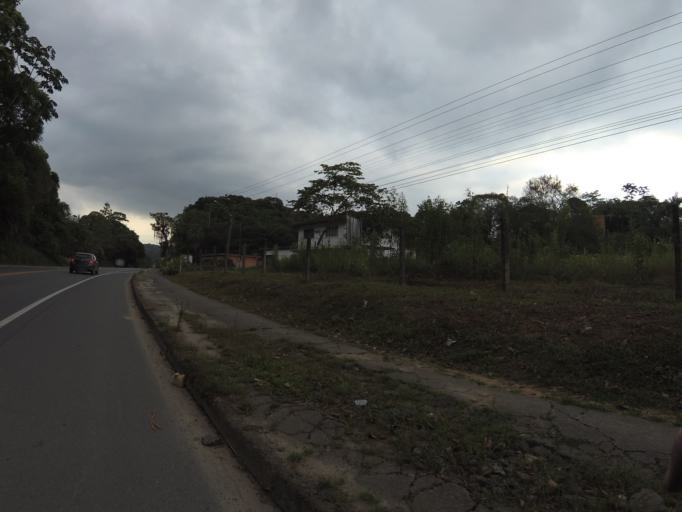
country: BR
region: Santa Catarina
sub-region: Indaial
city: Indaial
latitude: -26.8533
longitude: -49.1511
